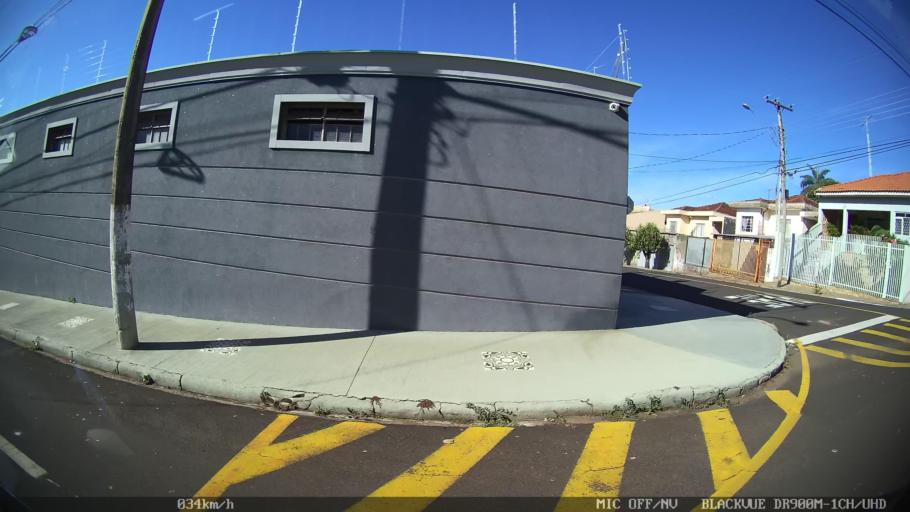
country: BR
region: Sao Paulo
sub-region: Franca
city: Franca
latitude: -20.5428
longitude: -47.4098
